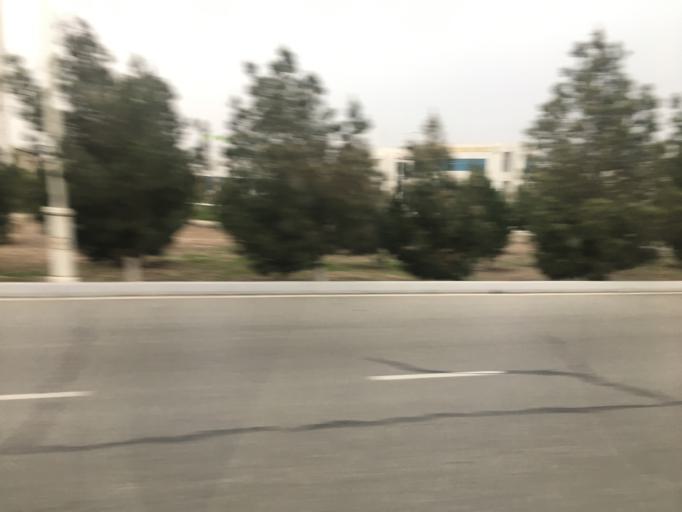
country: TM
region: Lebap
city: Turkmenabat
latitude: 39.0436
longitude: 63.5884
